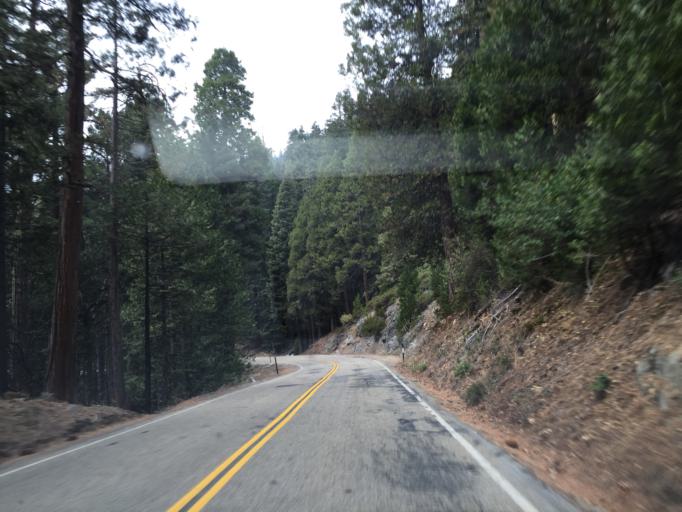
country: US
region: California
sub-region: Tulare County
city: Three Rivers
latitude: 36.7182
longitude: -118.9281
